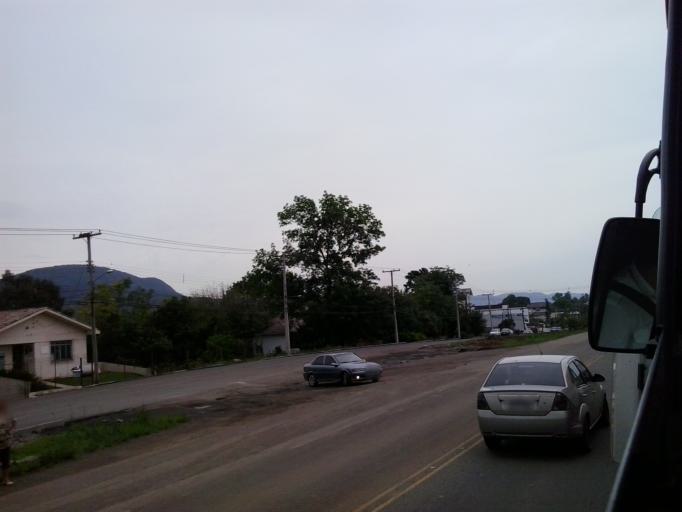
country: BR
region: Rio Grande do Sul
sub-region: Santa Maria
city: Santa Maria
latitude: -29.6945
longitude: -53.7462
